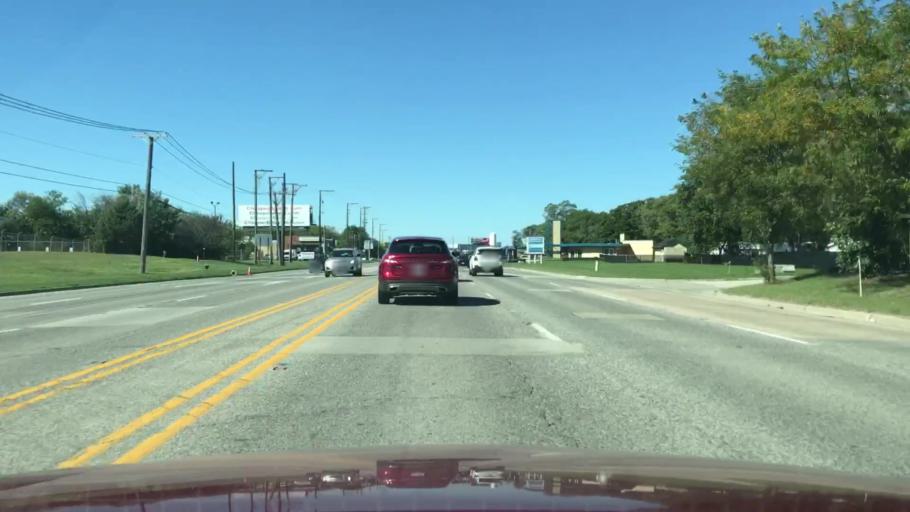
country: US
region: Illinois
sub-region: Cook County
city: Elk Grove Village
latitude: 42.0082
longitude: -87.9308
